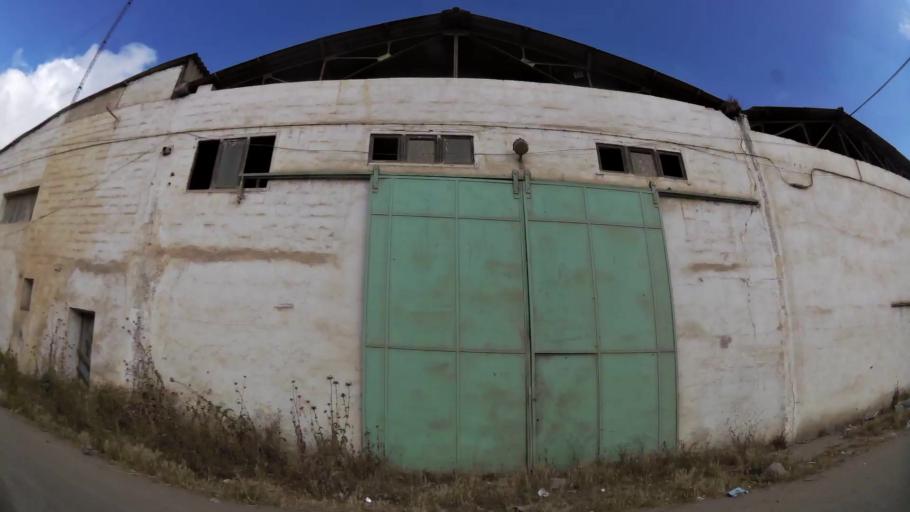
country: MA
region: Gharb-Chrarda-Beni Hssen
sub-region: Kenitra Province
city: Kenitra
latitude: 34.2701
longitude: -6.5668
